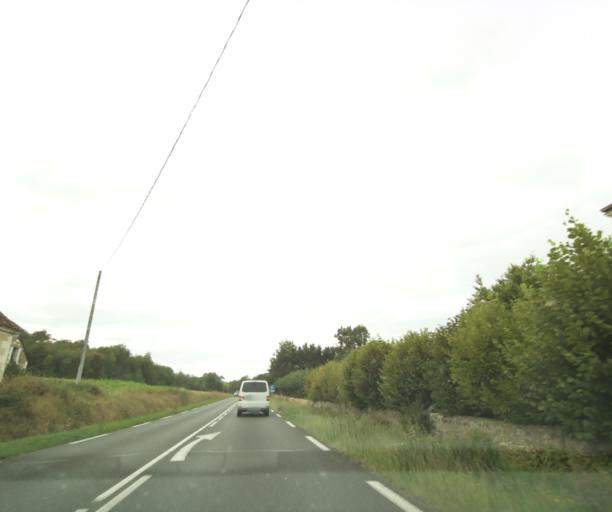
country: FR
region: Centre
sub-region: Departement d'Indre-et-Loire
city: Perrusson
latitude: 47.0711
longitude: 1.0746
